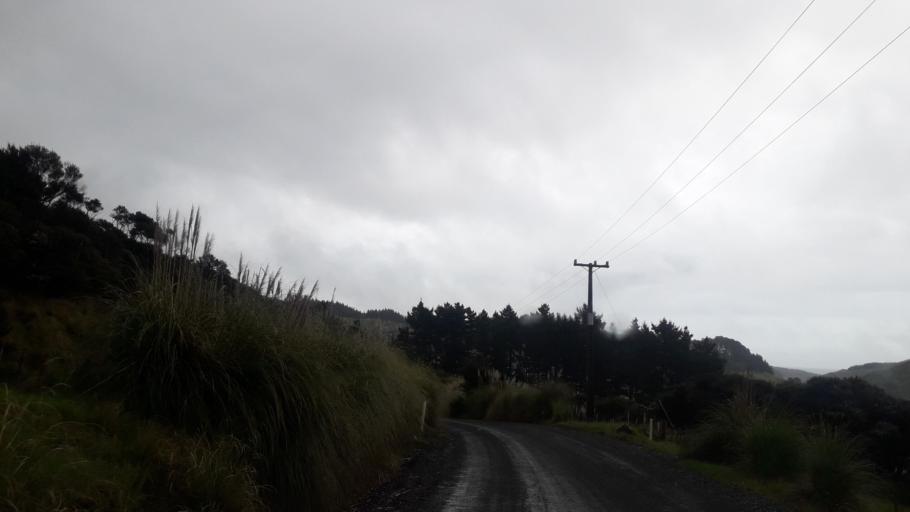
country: NZ
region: Northland
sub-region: Far North District
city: Ahipara
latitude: -35.4342
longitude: 173.3321
